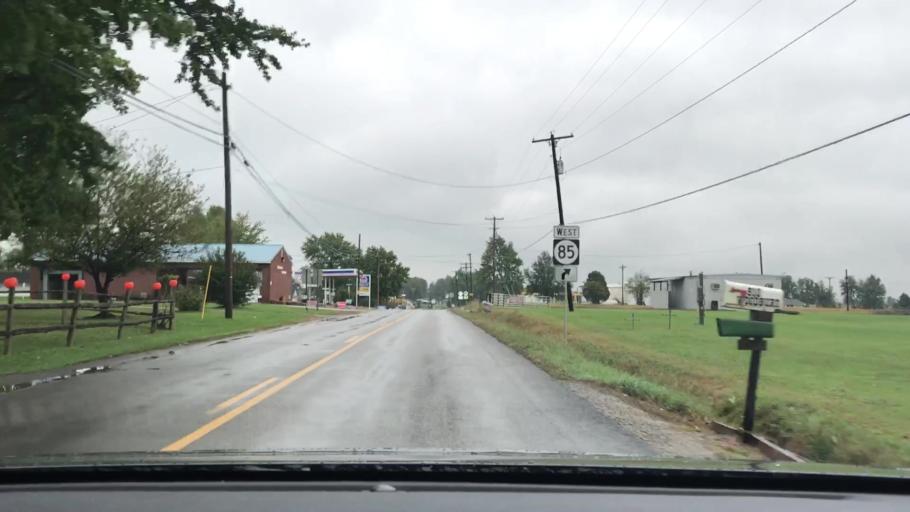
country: US
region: Kentucky
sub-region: McLean County
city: Calhoun
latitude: 37.4077
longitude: -87.2624
